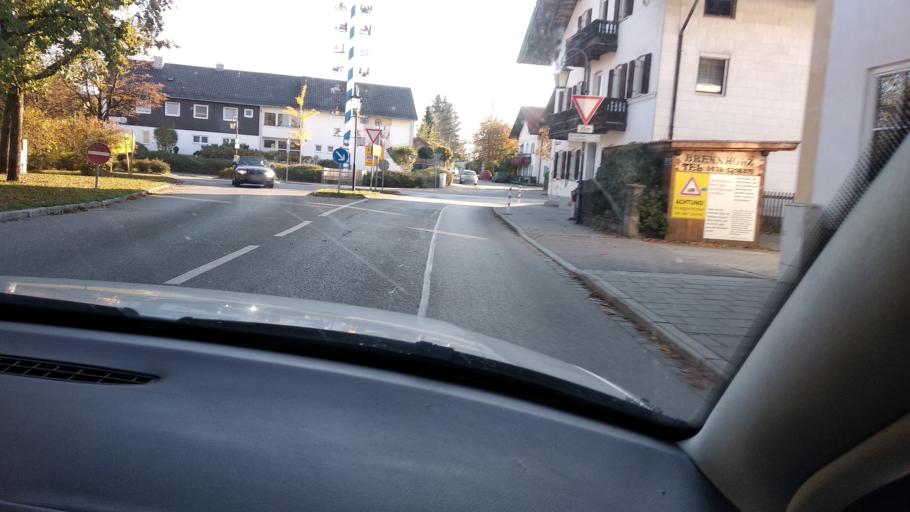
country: DE
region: Bavaria
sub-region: Upper Bavaria
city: Hohenkirchen-Siegertsbrunn
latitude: 48.0204
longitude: 11.7286
